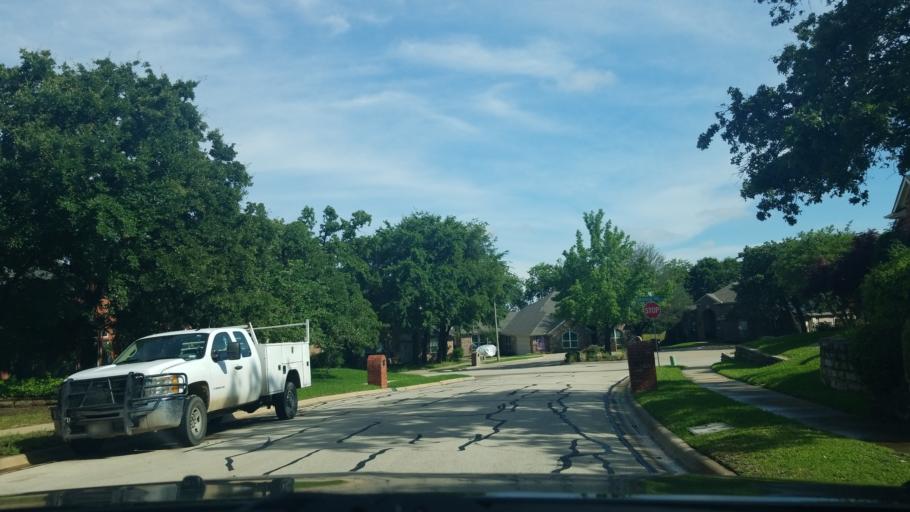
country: US
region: Texas
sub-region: Denton County
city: Denton
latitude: 33.1801
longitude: -97.1084
